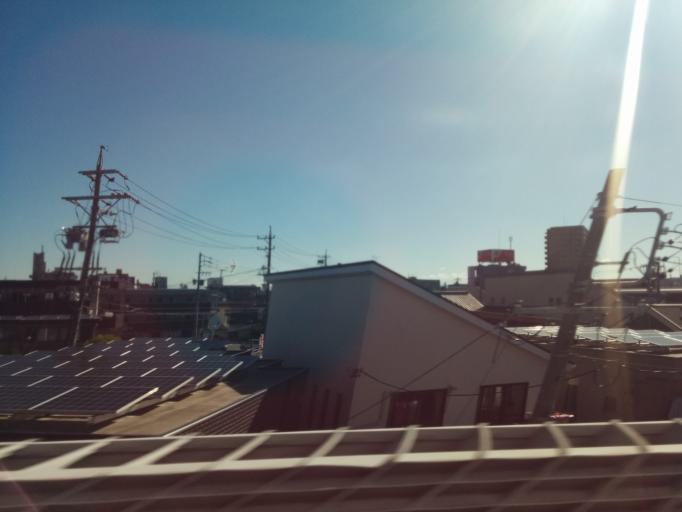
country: JP
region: Aichi
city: Anjo
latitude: 34.9563
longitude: 137.0722
